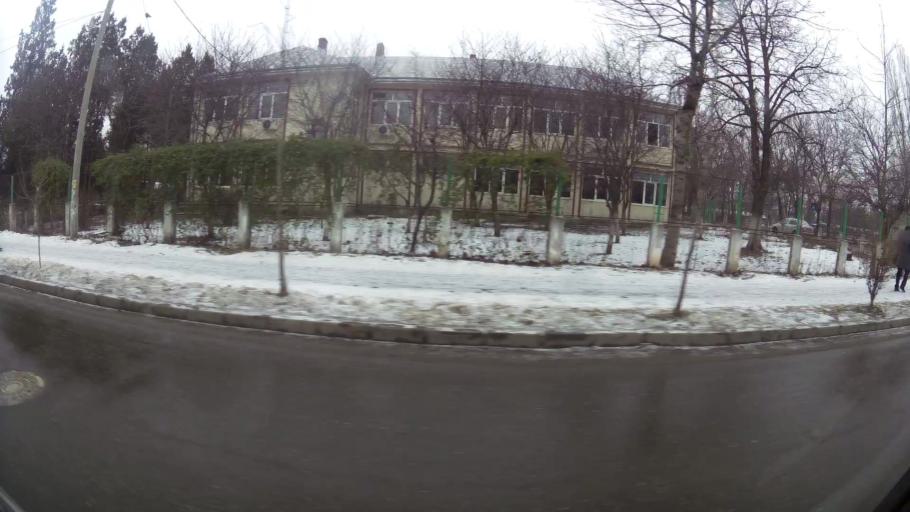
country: RO
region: Prahova
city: Ploiesti
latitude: 44.9520
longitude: 26.0455
